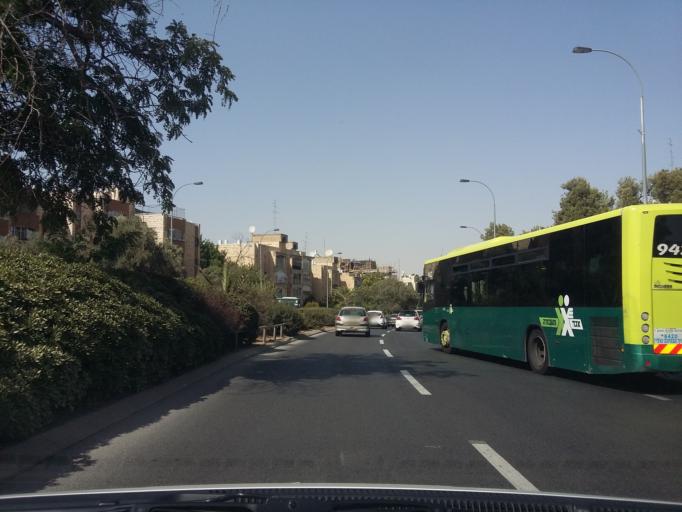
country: IL
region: Jerusalem
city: West Jerusalem
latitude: 31.7984
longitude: 35.2234
